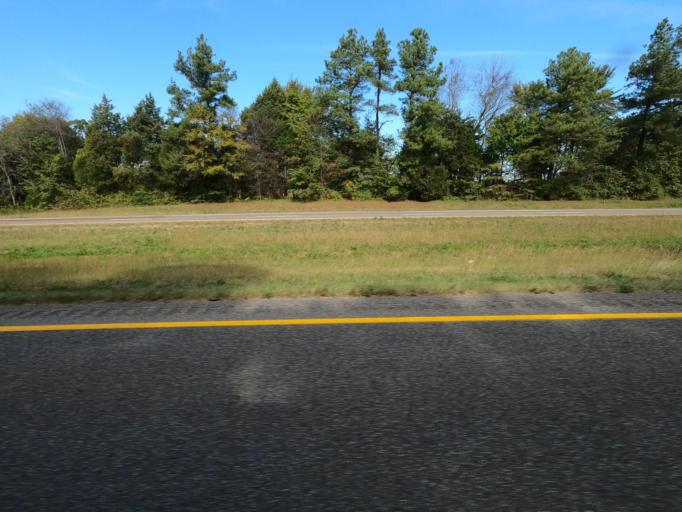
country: US
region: Tennessee
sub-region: Haywood County
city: Brownsville
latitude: 35.5760
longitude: -89.1240
